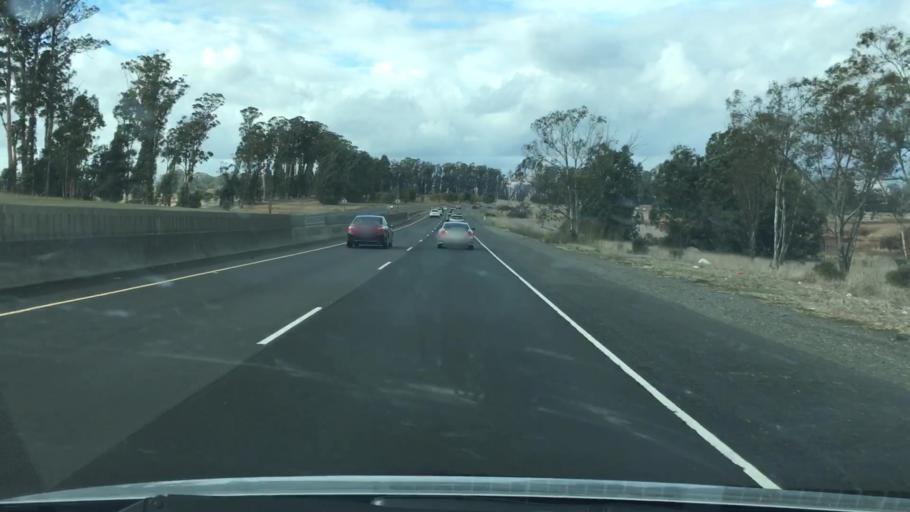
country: US
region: California
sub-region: Napa County
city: Napa
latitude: 38.2481
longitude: -122.2959
